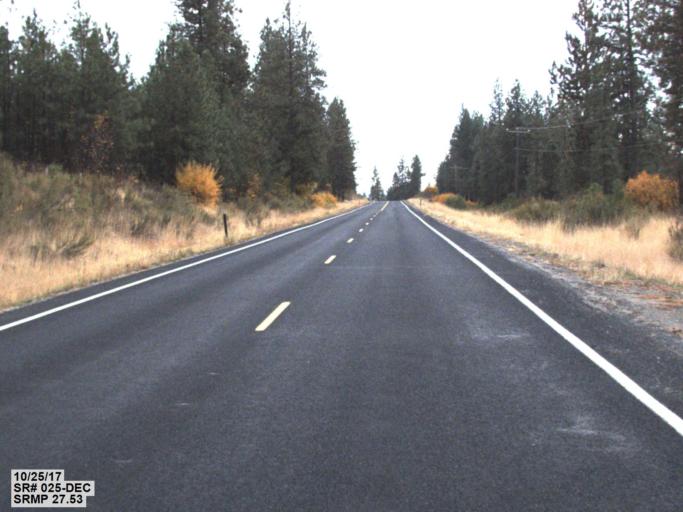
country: US
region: Washington
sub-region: Lincoln County
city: Davenport
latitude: 47.9498
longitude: -118.3140
